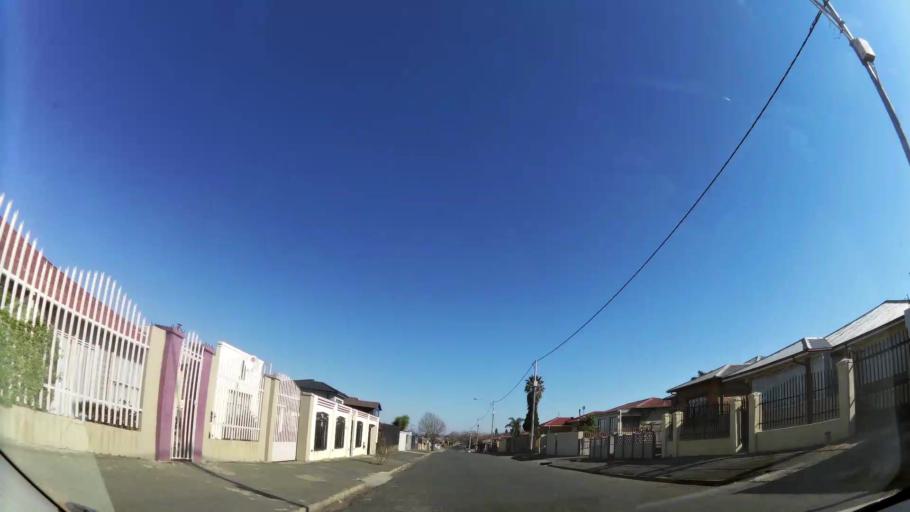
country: ZA
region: Gauteng
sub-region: City of Johannesburg Metropolitan Municipality
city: Johannesburg
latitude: -26.1978
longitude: 27.9955
